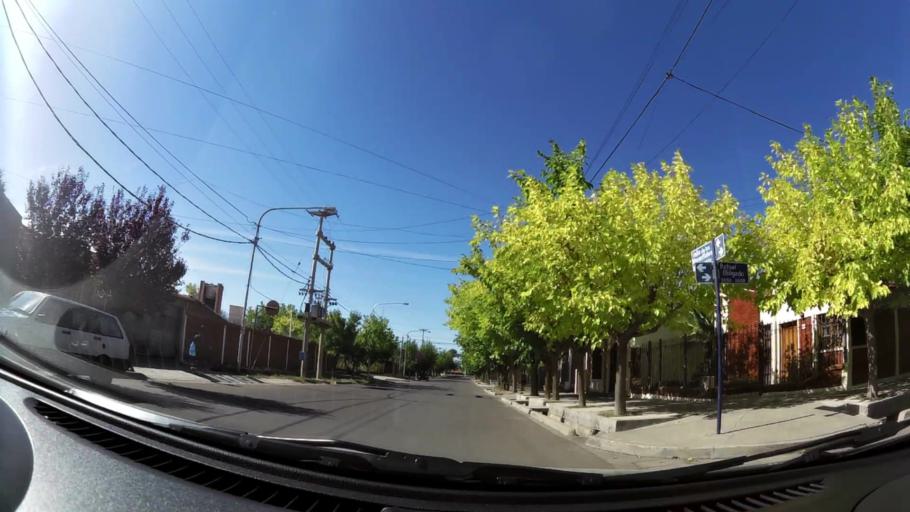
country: AR
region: Mendoza
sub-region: Departamento de Godoy Cruz
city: Godoy Cruz
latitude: -32.9471
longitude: -68.8117
